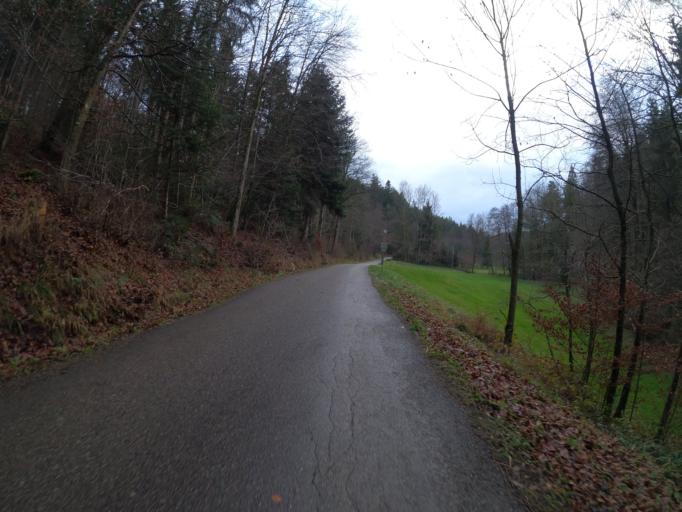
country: DE
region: Baden-Wuerttemberg
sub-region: Regierungsbezirk Stuttgart
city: Lorch
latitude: 48.7817
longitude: 9.7221
